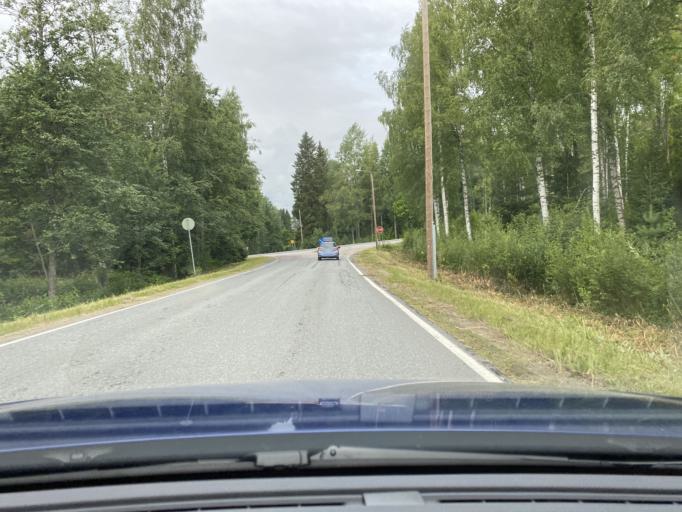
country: FI
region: Pirkanmaa
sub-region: Ylae-Pirkanmaa
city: Maenttae
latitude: 62.0230
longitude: 24.6943
